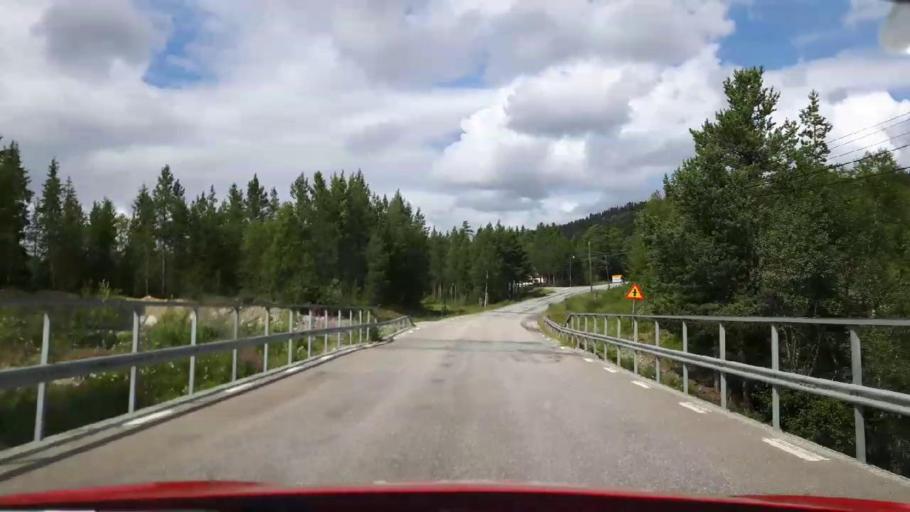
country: NO
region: Hedmark
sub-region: Engerdal
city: Engerdal
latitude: 62.4358
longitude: 12.6783
